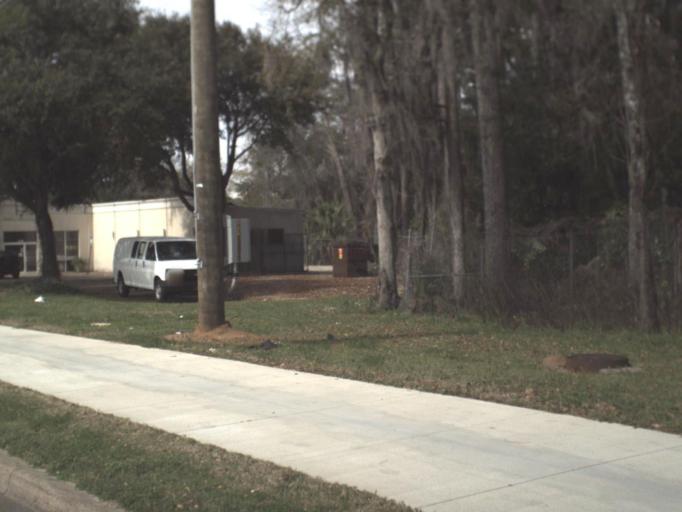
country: US
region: Florida
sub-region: Leon County
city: Tallahassee
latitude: 30.4471
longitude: -84.3197
